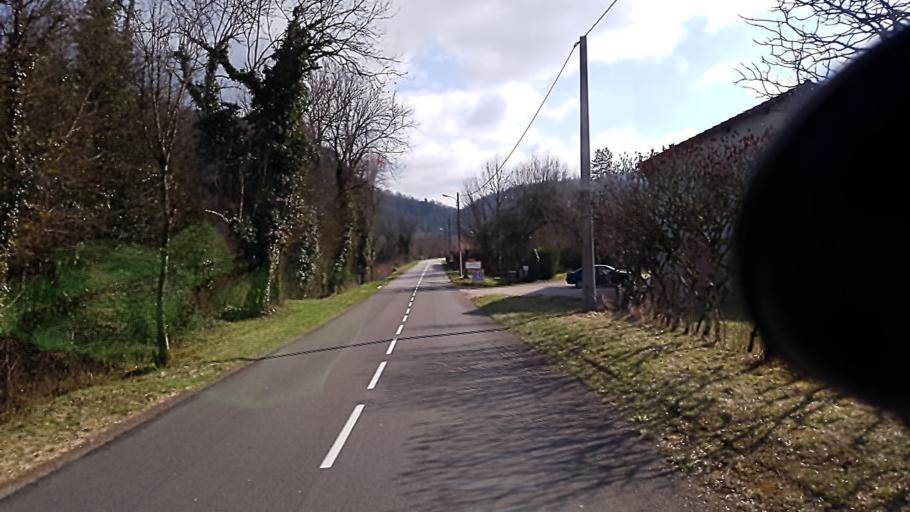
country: FR
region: Rhone-Alpes
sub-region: Departement de l'Ain
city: Dortan
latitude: 46.3371
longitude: 5.6476
